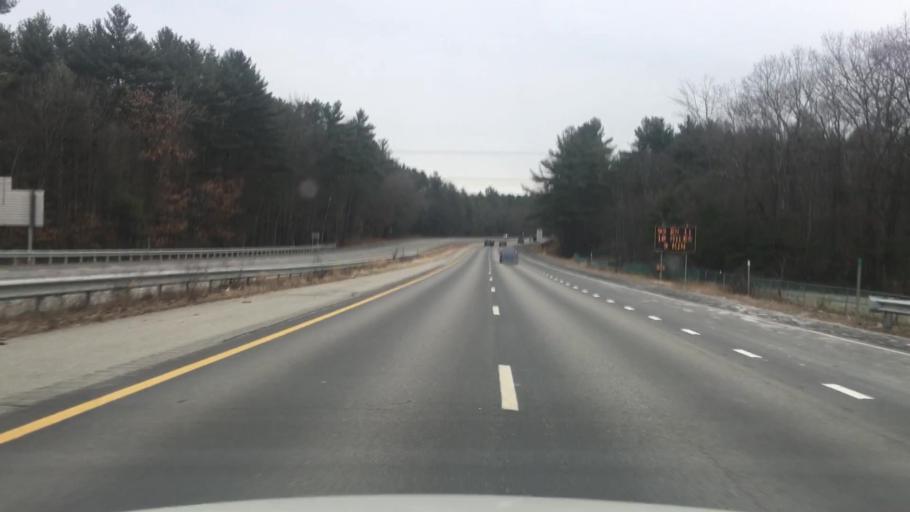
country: US
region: New Hampshire
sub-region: Merrimack County
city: Concord
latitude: 43.1829
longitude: -71.5935
